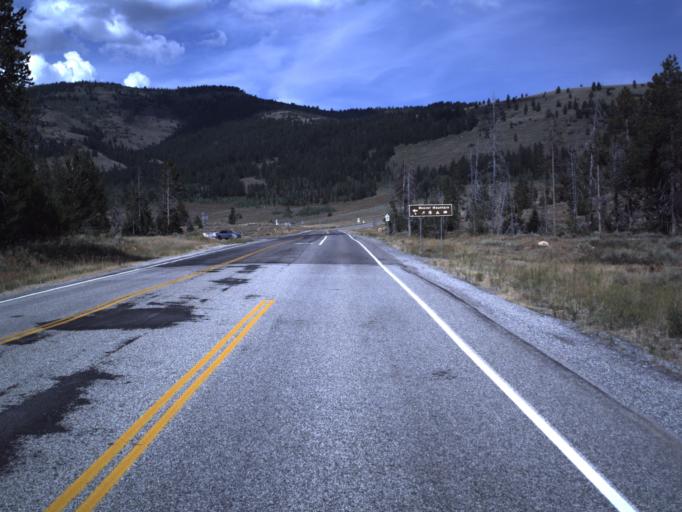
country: US
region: Utah
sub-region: Cache County
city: Richmond
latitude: 41.9622
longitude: -111.5326
